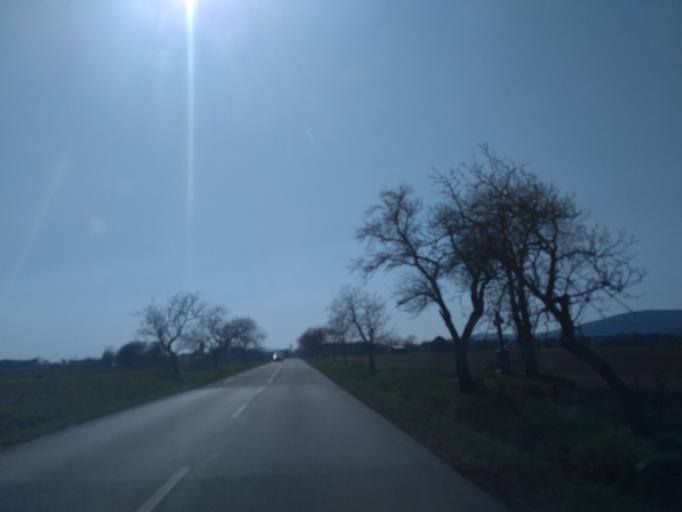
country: SK
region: Kosicky
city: Secovce
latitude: 48.6858
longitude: 21.6220
